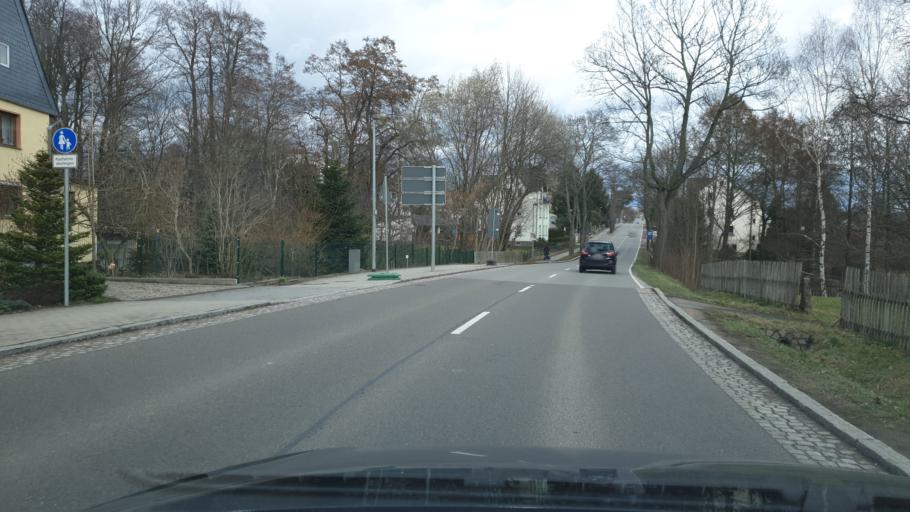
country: DE
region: Saxony
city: Claussnitz
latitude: 50.9368
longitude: 12.8823
